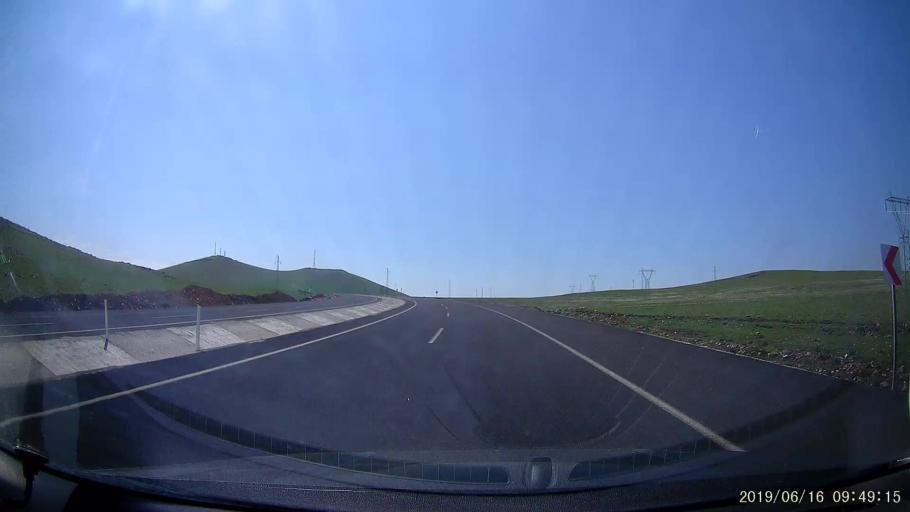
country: TR
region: Kars
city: Digor
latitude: 40.4233
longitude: 43.3571
